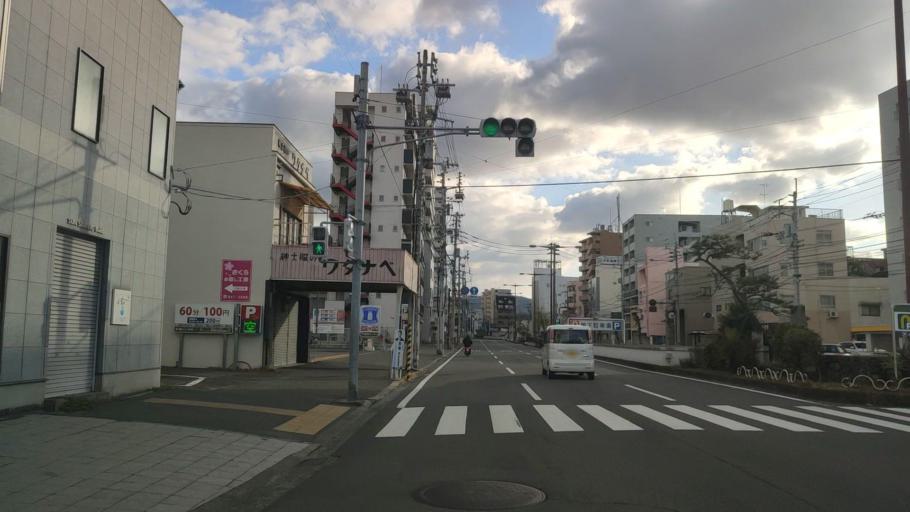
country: JP
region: Ehime
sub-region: Shikoku-chuo Shi
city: Matsuyama
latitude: 33.8352
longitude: 132.7678
